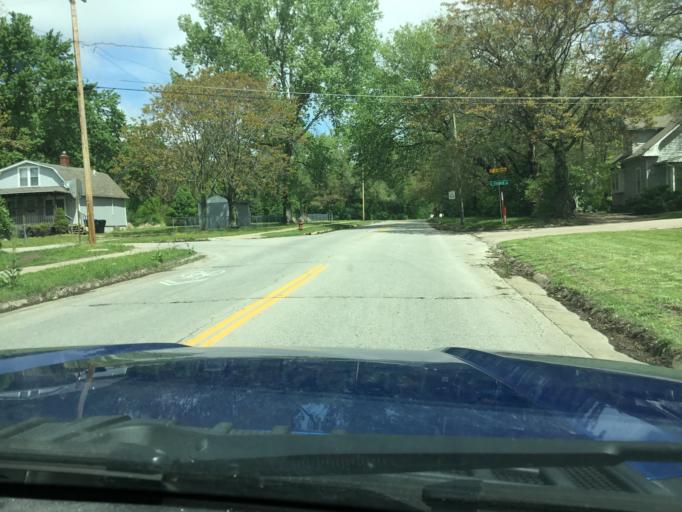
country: US
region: Kansas
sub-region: Shawnee County
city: Topeka
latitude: 39.0553
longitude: -95.6426
